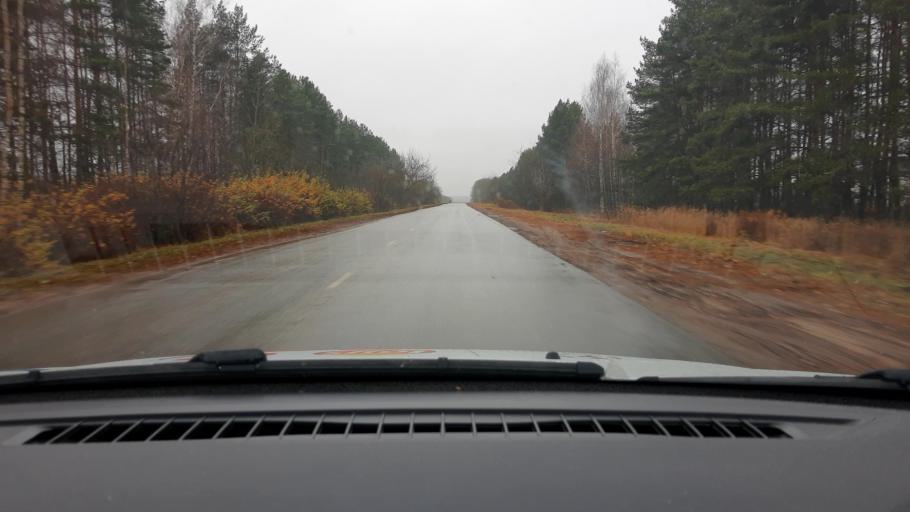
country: RU
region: Nizjnij Novgorod
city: Burevestnik
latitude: 56.0654
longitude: 43.8851
